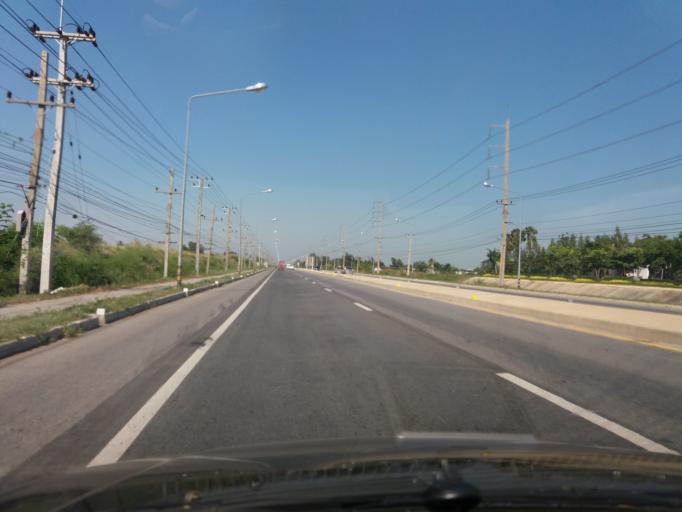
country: TH
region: Chai Nat
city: Manorom
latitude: 15.2805
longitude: 100.0959
